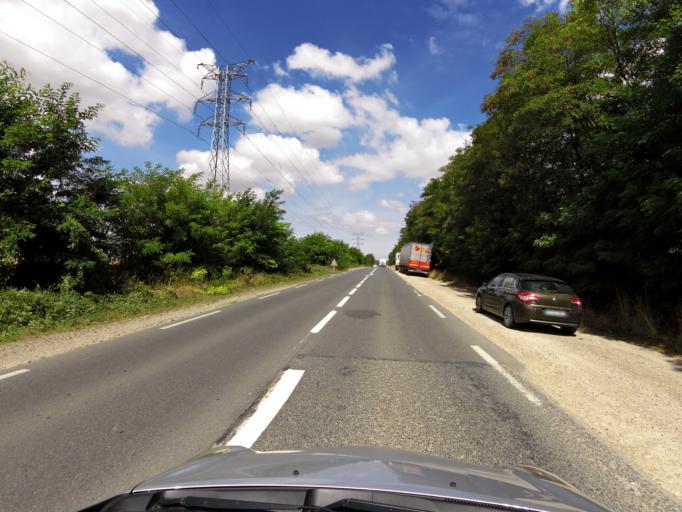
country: FR
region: Ile-de-France
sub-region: Departement de Seine-et-Marne
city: Chauconin-Neufmontiers
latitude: 48.9651
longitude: 2.8600
